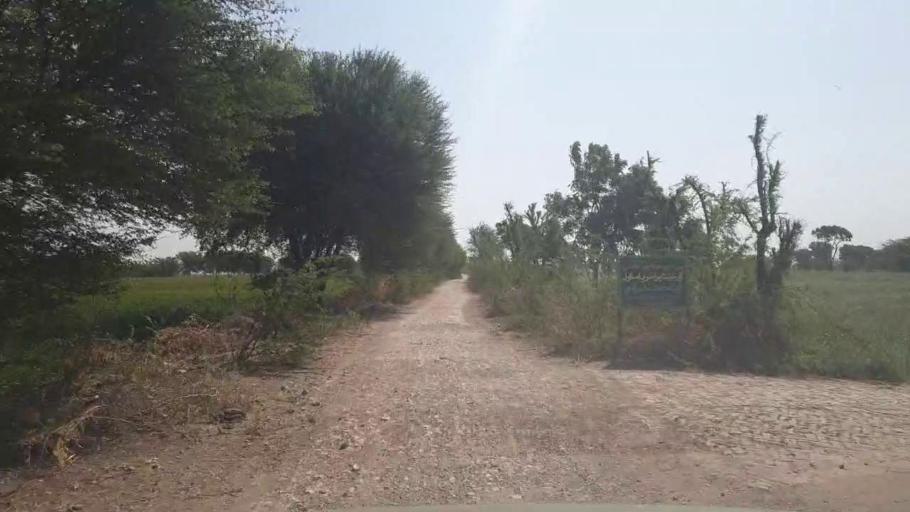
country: PK
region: Sindh
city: Kunri
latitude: 25.2704
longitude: 69.6345
